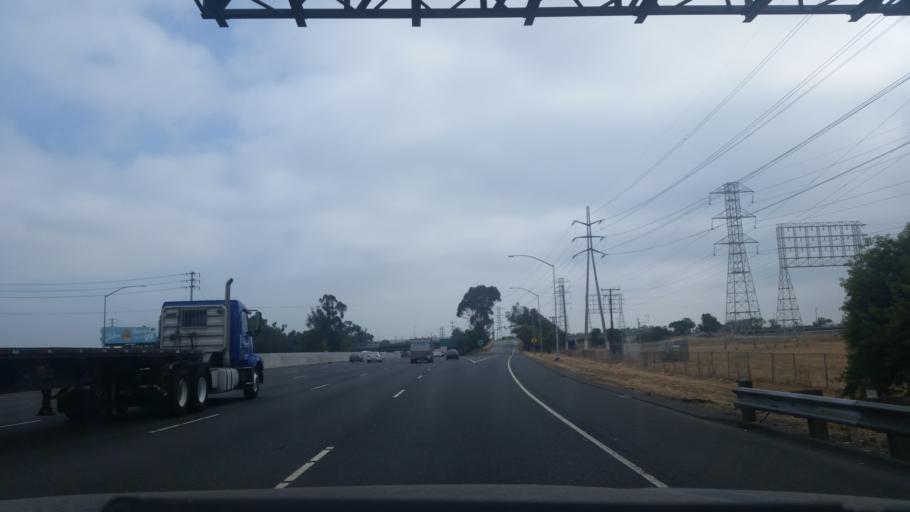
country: US
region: California
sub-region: Los Angeles County
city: East Rancho Dominguez
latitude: 33.8589
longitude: -118.2016
